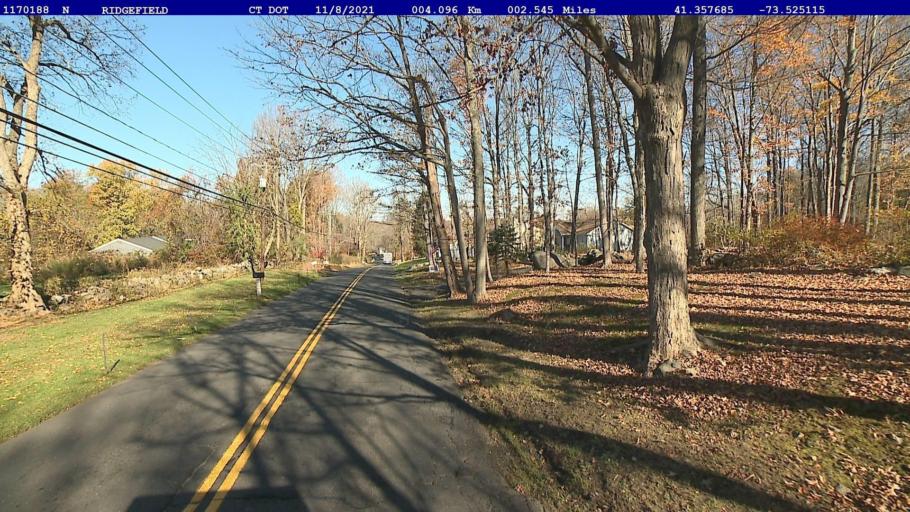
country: US
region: New York
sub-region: Putnam County
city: Peach Lake
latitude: 41.3577
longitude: -73.5251
